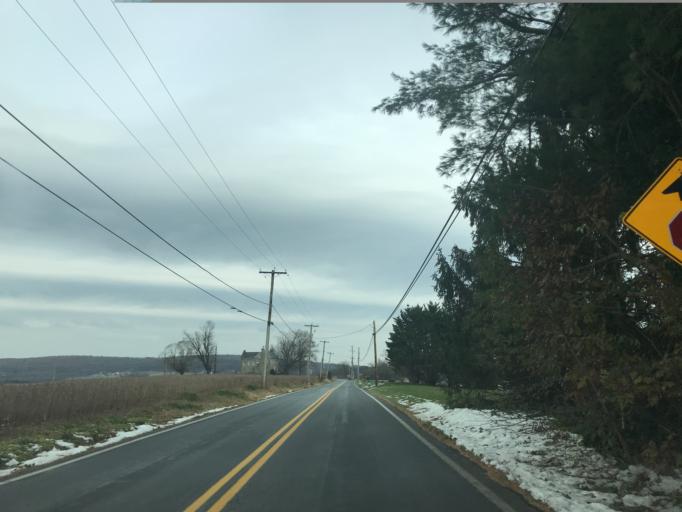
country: US
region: Pennsylvania
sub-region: York County
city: Susquehanna Trails
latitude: 39.6920
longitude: -76.3926
